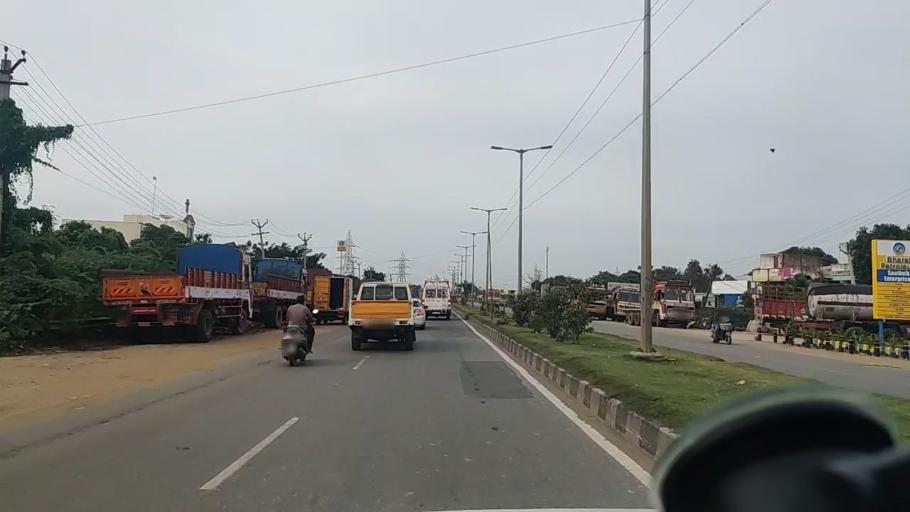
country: IN
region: Tamil Nadu
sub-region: Thiruvallur
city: Chinnasekkadu
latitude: 13.1664
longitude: 80.2290
